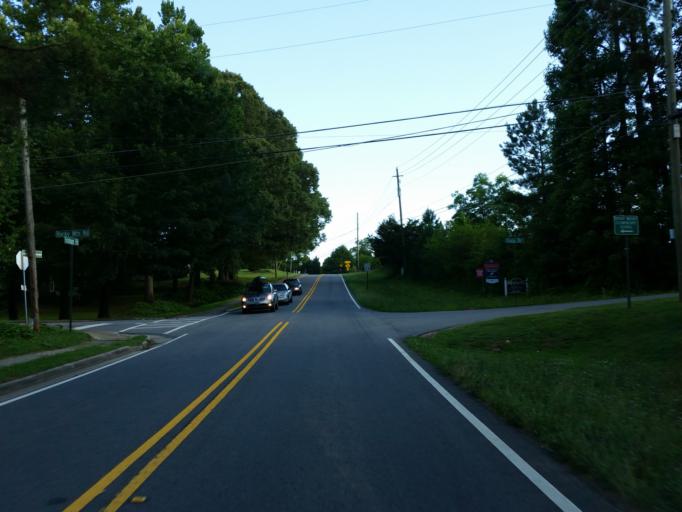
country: US
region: Georgia
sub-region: Cherokee County
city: Woodstock
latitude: 34.0496
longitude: -84.4849
